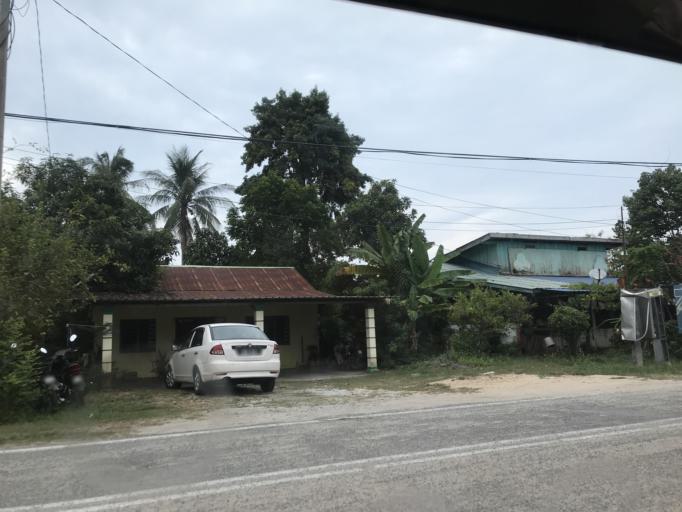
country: MY
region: Kelantan
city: Kota Bharu
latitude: 6.1439
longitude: 102.2268
